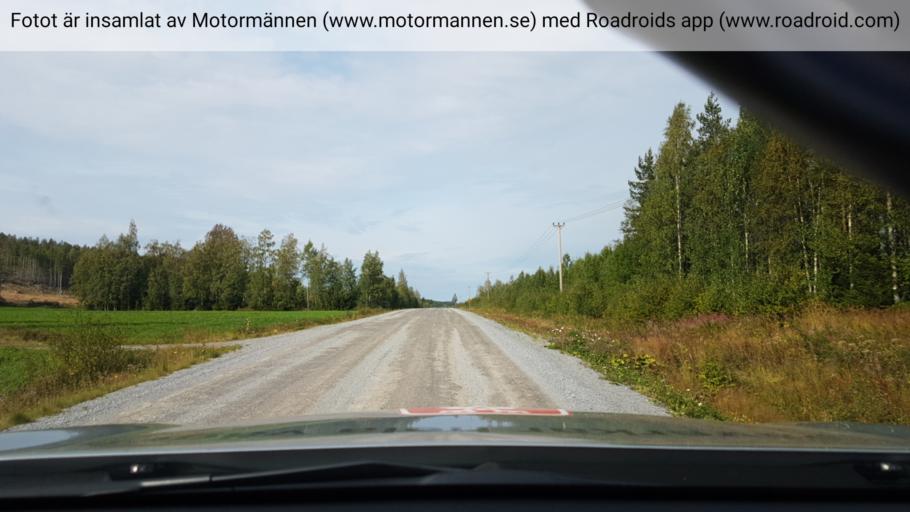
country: SE
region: Vaesterbotten
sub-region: Bjurholms Kommun
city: Bjurholm
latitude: 63.8732
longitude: 19.4532
